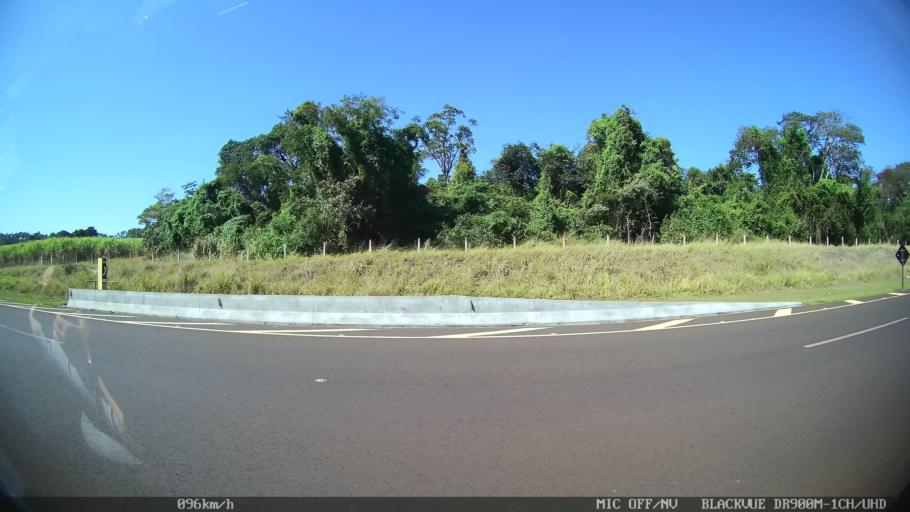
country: BR
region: Sao Paulo
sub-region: Franca
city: Franca
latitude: -20.6519
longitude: -47.4868
